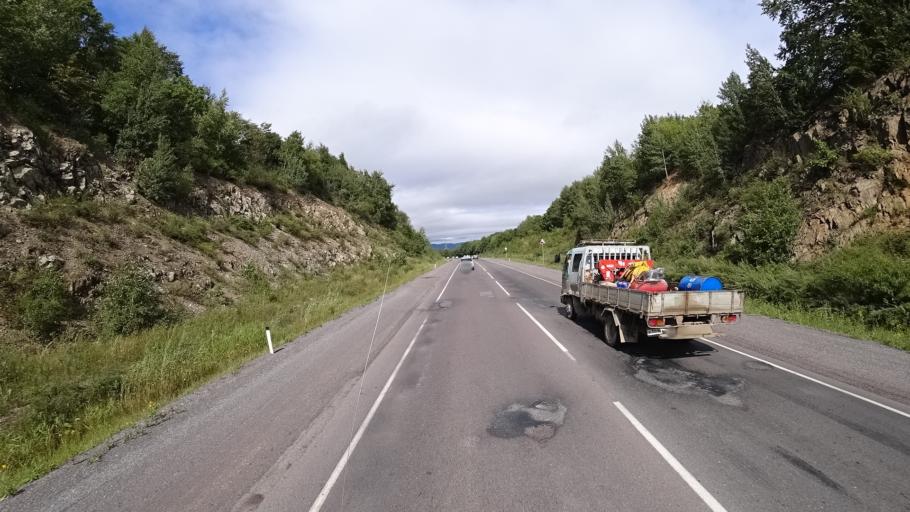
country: RU
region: Primorskiy
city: Lyalichi
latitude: 44.1285
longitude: 132.4258
